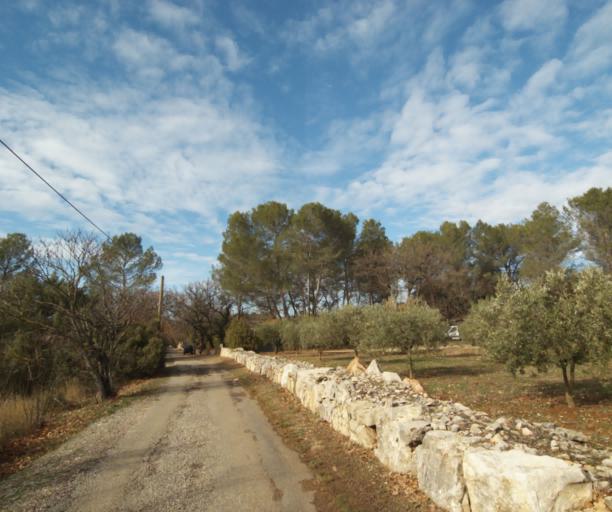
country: FR
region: Provence-Alpes-Cote d'Azur
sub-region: Departement du Var
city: Trans-en-Provence
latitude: 43.5204
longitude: 6.5064
